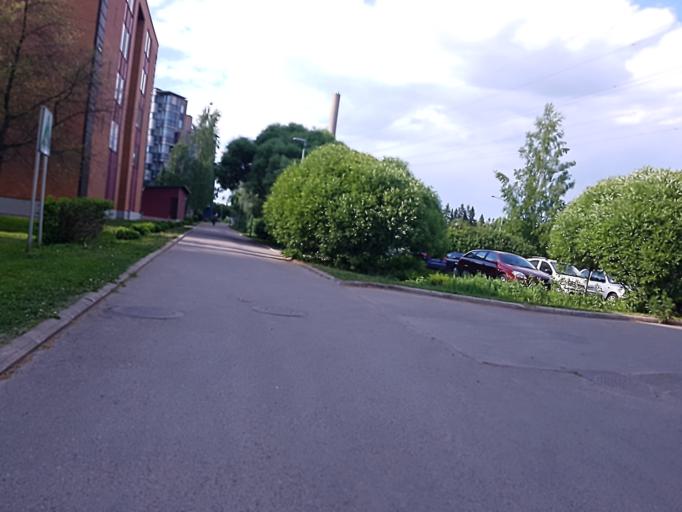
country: FI
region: Uusimaa
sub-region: Helsinki
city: Helsinki
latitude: 60.2335
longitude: 24.9821
